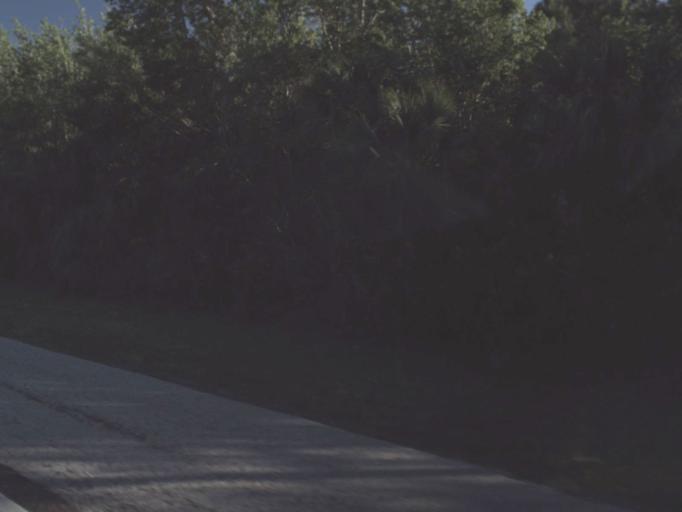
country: US
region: Florida
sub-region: Flagler County
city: Palm Coast
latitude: 29.5834
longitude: -81.2383
